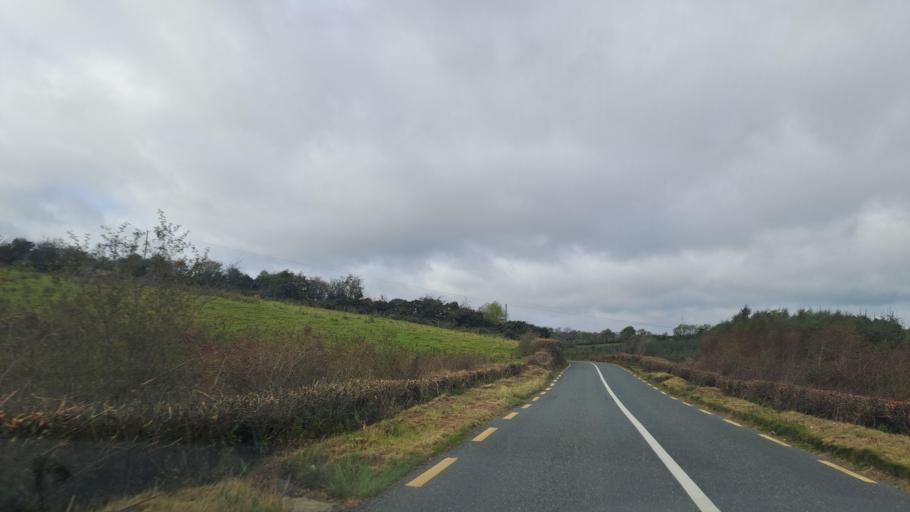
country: IE
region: Ulster
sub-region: An Cabhan
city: Bailieborough
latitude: 53.9329
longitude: -6.9073
